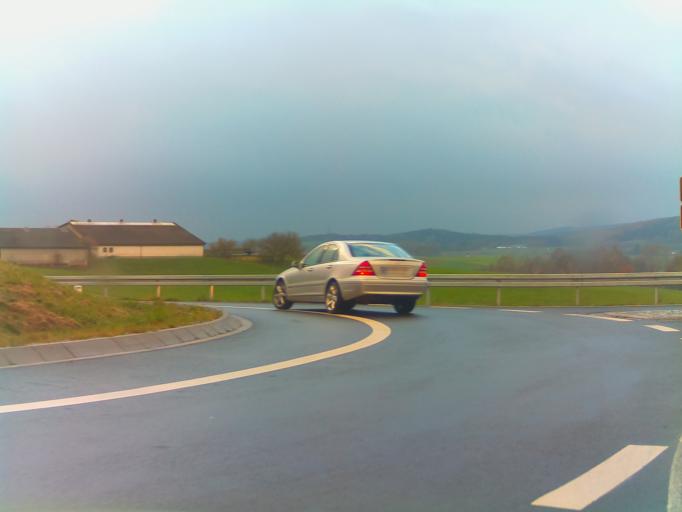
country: DE
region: Hesse
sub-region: Regierungsbezirk Kassel
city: Neuhof
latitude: 50.4471
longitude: 9.6088
